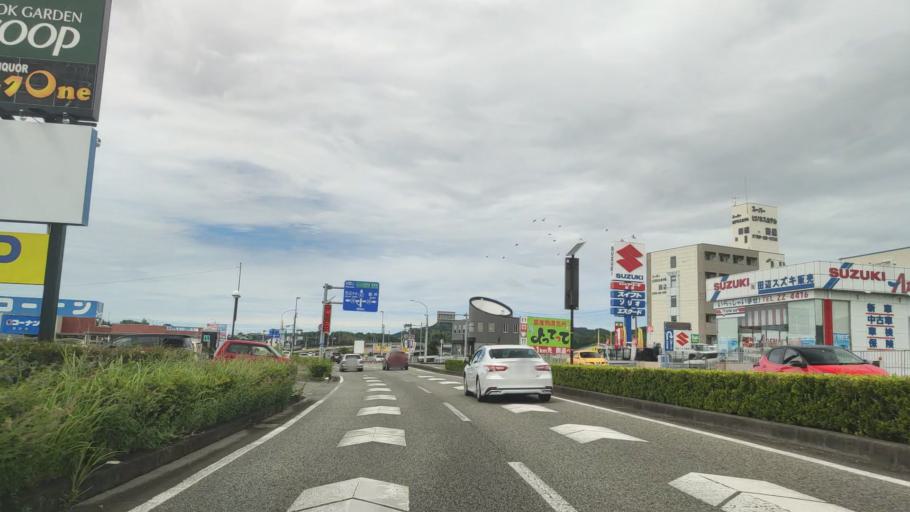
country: JP
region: Wakayama
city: Tanabe
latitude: 33.7406
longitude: 135.3919
